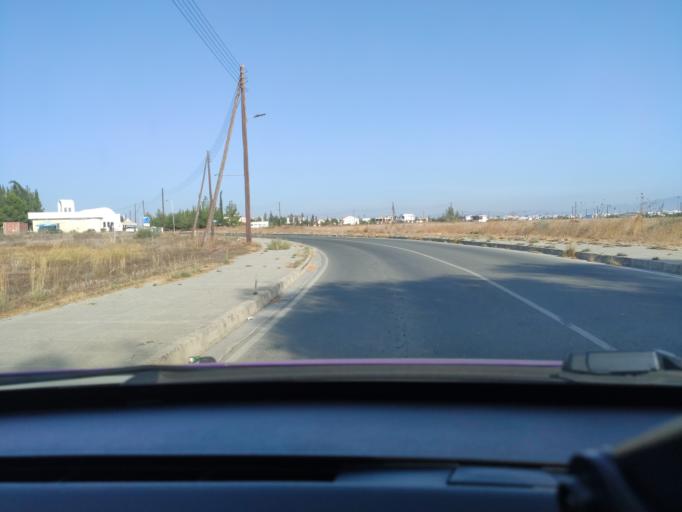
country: CY
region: Lefkosia
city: Tseri
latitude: 35.1066
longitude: 33.3563
